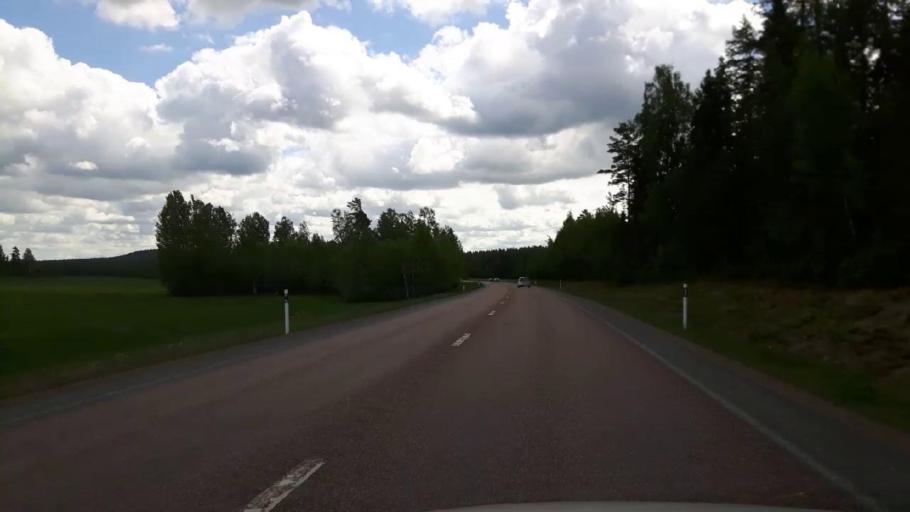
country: SE
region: Dalarna
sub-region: Faluns Kommun
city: Falun
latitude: 60.5044
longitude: 15.7408
